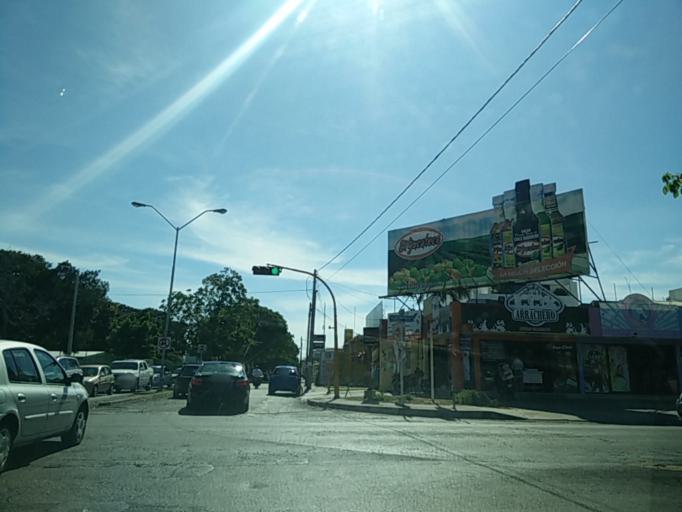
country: MX
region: Yucatan
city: Merida
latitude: 21.0015
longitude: -89.6054
